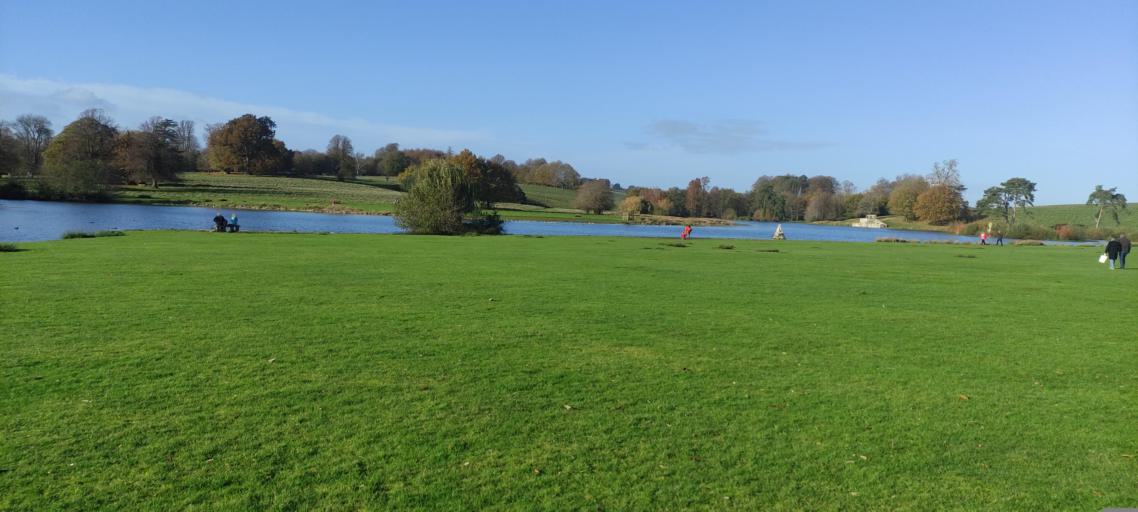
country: GB
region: England
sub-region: West Sussex
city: Petworth
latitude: 50.9882
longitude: -0.6159
